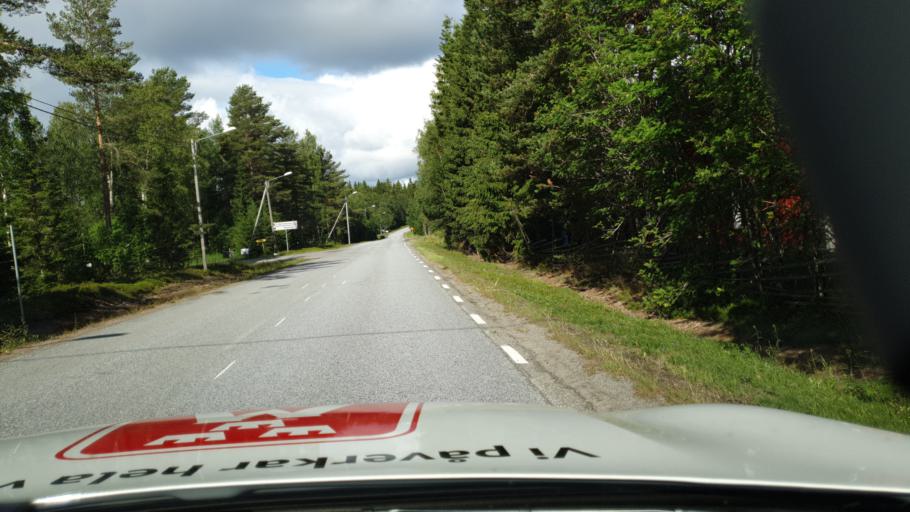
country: SE
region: Vaesterbotten
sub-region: Umea Kommun
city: Roback
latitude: 63.6736
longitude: 20.1187
